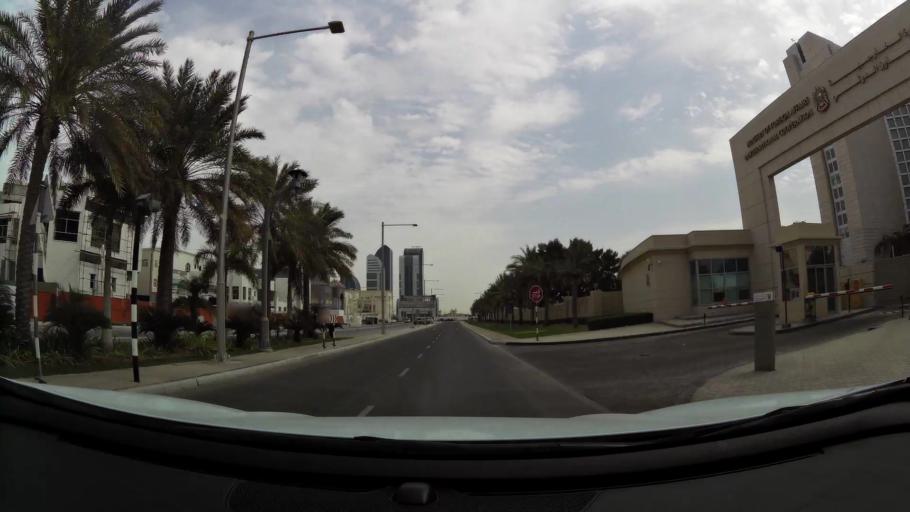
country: AE
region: Abu Dhabi
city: Abu Dhabi
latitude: 24.4551
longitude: 54.3322
